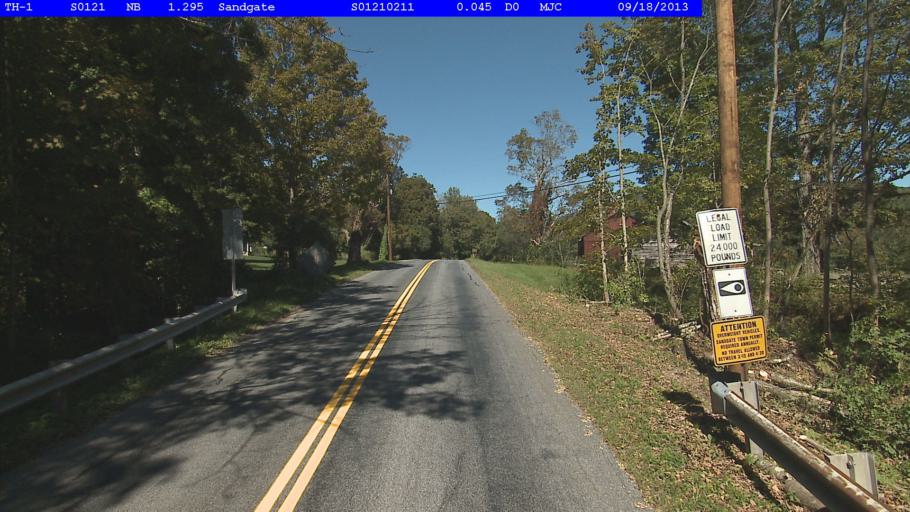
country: US
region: Vermont
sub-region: Bennington County
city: Arlington
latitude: 43.1213
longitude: -73.2076
